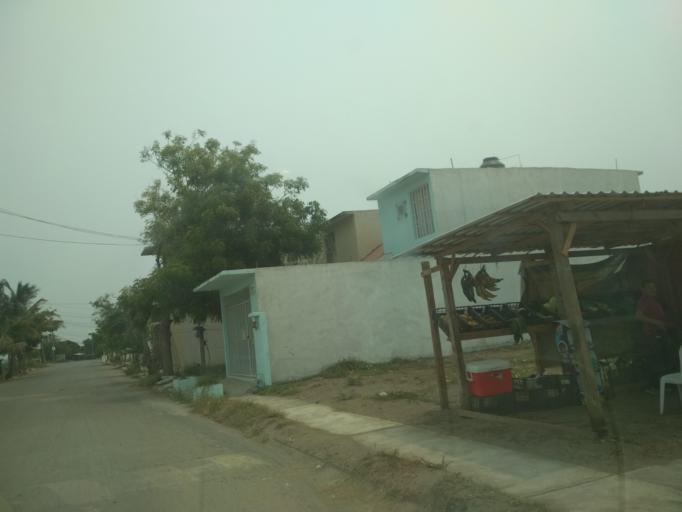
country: MX
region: Veracruz
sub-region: Veracruz
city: Arboledas
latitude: 19.2079
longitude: -96.2148
